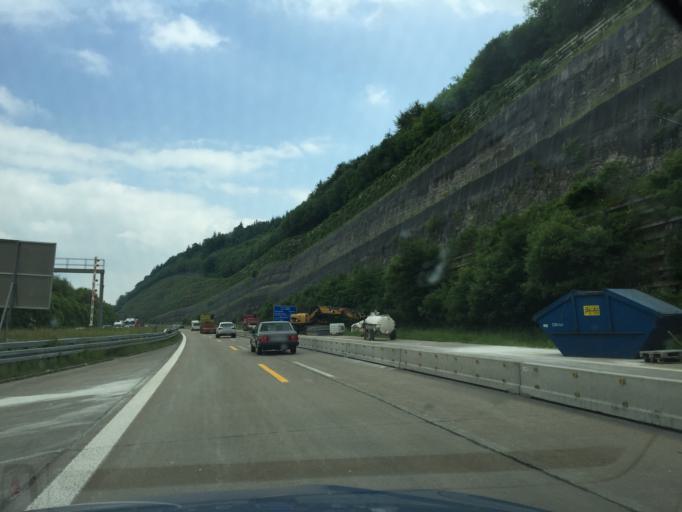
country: DE
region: Baden-Wuerttemberg
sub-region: Regierungsbezirk Stuttgart
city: Westhausen
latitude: 48.8682
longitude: 10.1753
